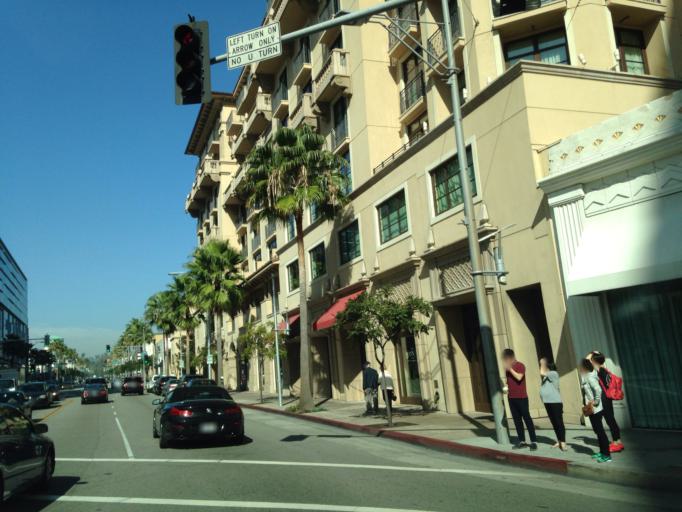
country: US
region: California
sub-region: Los Angeles County
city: Beverly Hills
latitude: 34.0670
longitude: -118.3991
